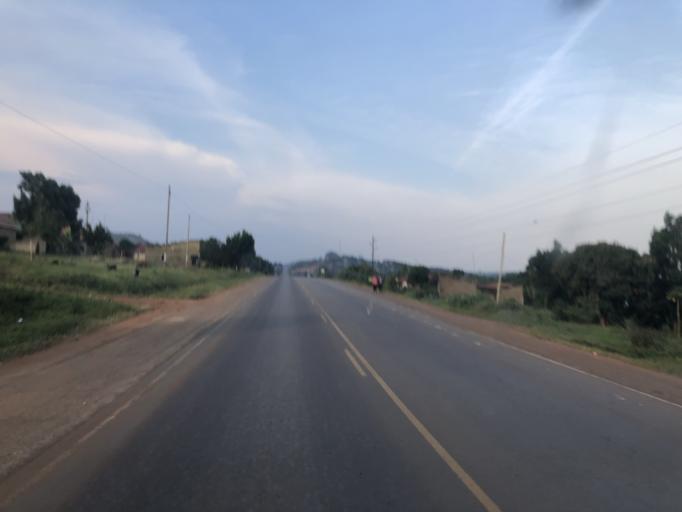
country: UG
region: Central Region
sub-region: Mpigi District
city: Mpigi
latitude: 0.2091
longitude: 32.3180
